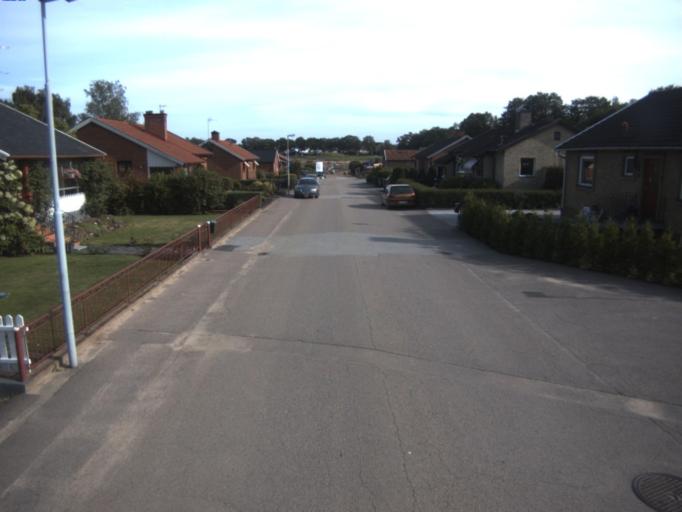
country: SE
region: Skane
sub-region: Helsingborg
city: Odakra
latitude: 56.1027
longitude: 12.7483
